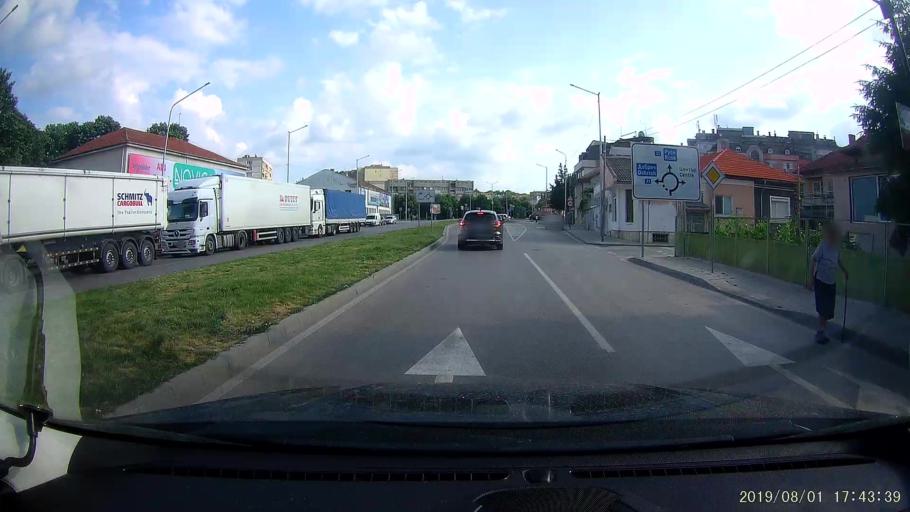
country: BG
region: Silistra
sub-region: Obshtina Silistra
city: Silistra
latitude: 44.1132
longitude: 27.2727
